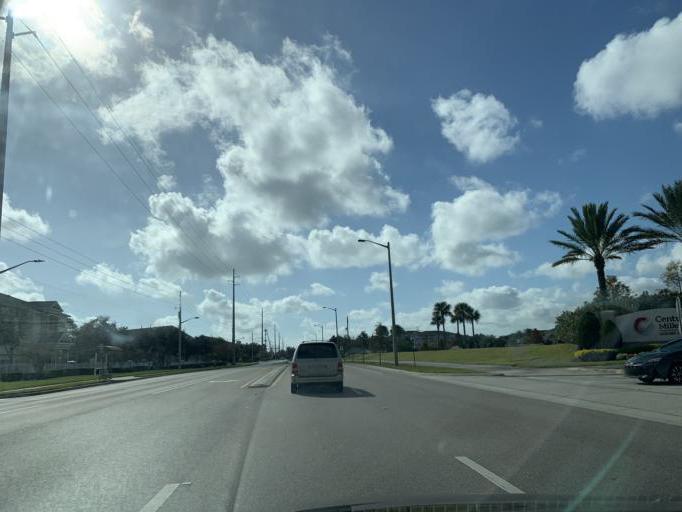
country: US
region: Florida
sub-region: Orange County
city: Oak Ridge
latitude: 28.4782
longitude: -81.4423
